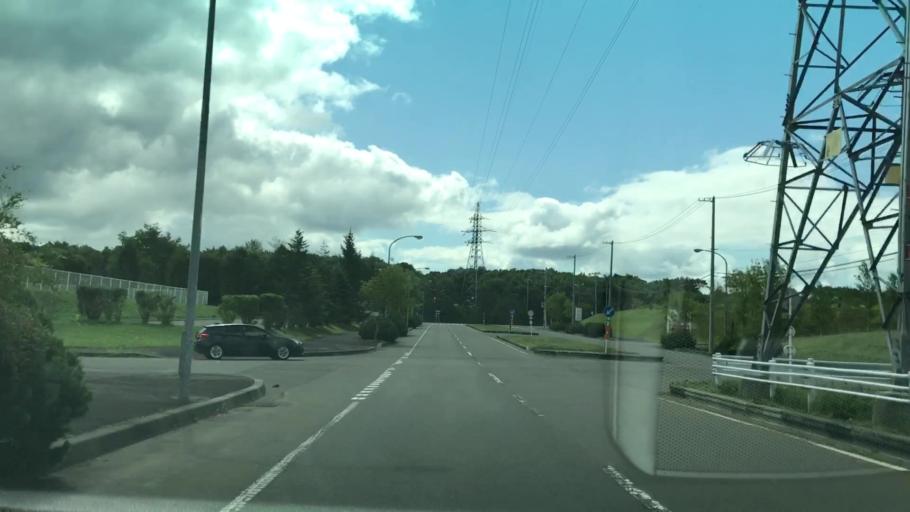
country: JP
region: Hokkaido
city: Chitose
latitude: 42.7742
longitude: 141.6166
